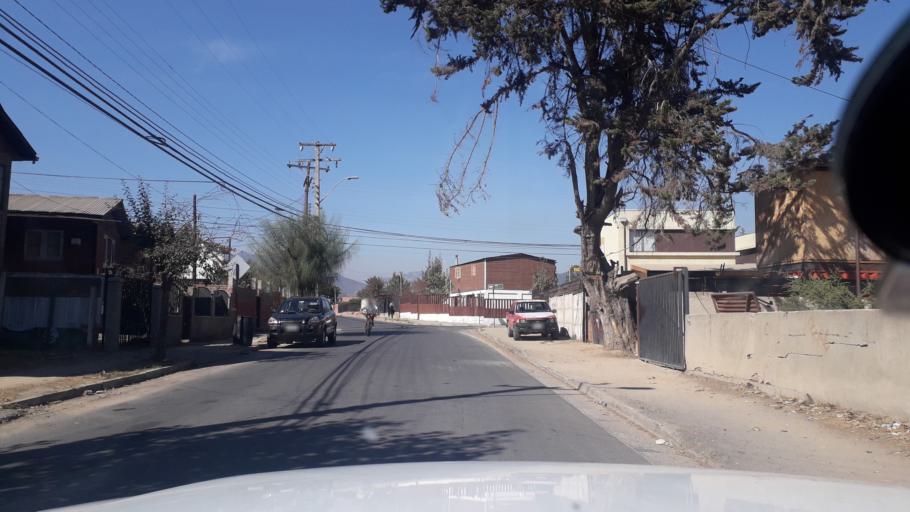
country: CL
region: Valparaiso
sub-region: Provincia de Marga Marga
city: Villa Alemana
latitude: -33.0432
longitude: -71.3517
